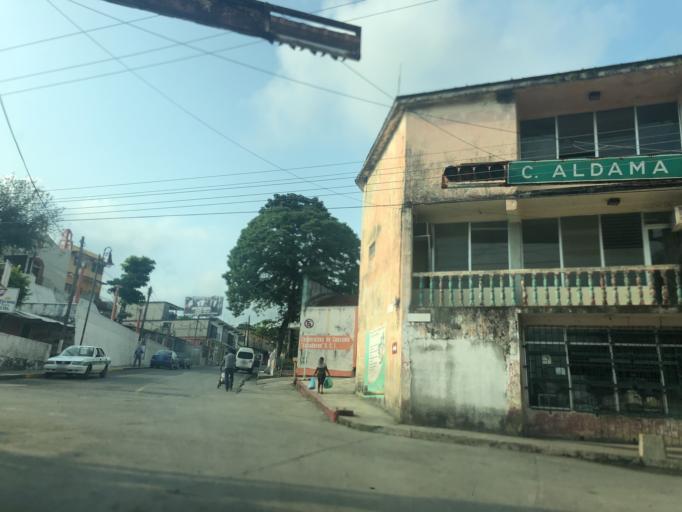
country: MX
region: Chiapas
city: Pichucalco
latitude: 17.5089
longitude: -93.1170
